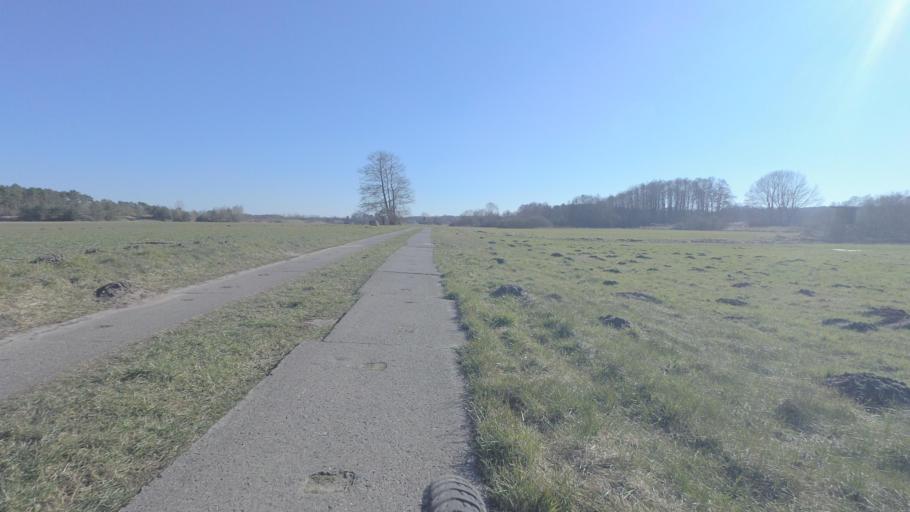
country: DE
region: Brandenburg
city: Rangsdorf
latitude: 52.2554
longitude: 13.4131
